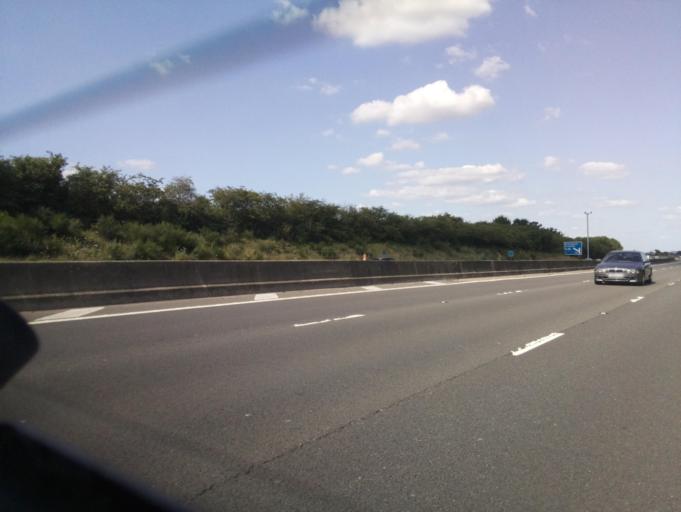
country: GB
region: England
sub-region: Worcestershire
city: Droitwich
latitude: 52.2684
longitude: -2.1300
